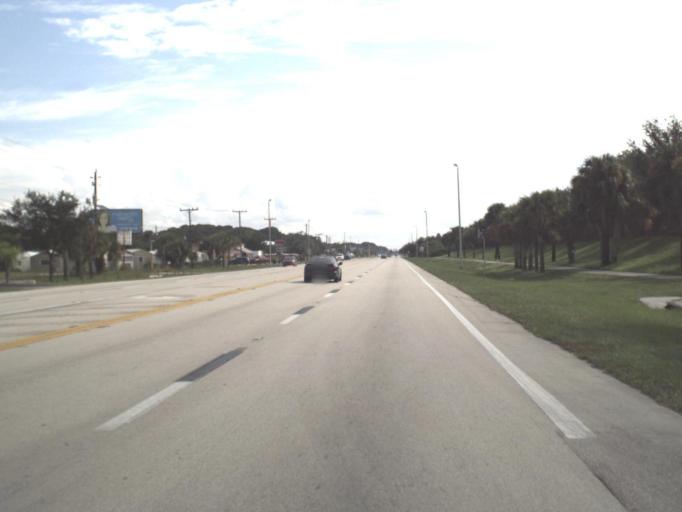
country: US
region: Florida
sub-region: Lee County
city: Fort Myers Shores
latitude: 26.7074
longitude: -81.7329
